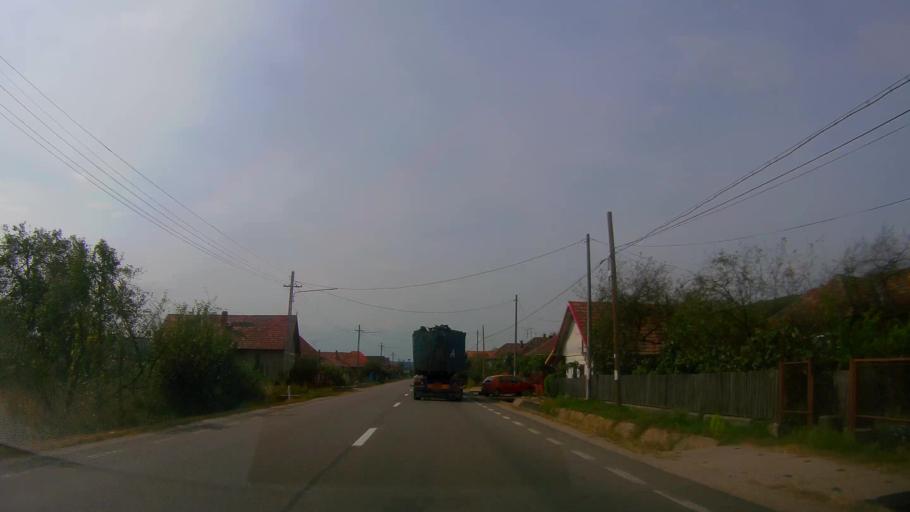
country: RO
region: Salaj
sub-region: Comuna Zimbor
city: Zimbor
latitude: 47.0088
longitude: 23.2615
